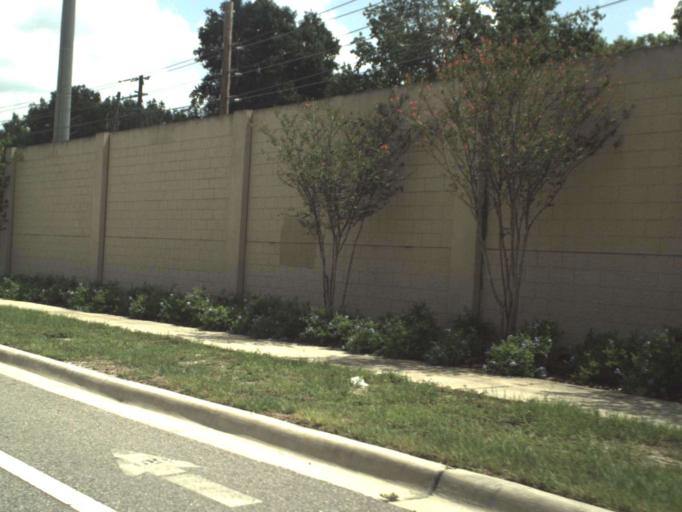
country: US
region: Florida
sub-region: Seminole County
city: Forest City
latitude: 28.6492
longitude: -81.4151
